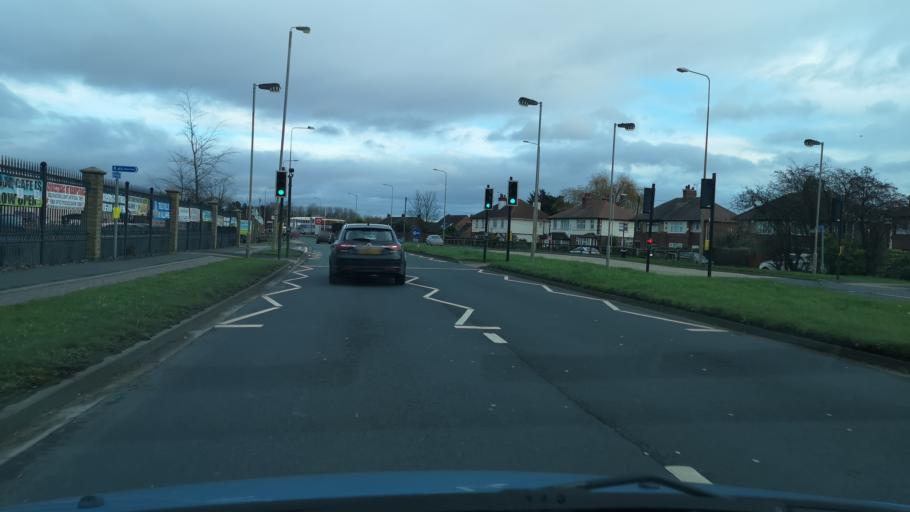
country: GB
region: England
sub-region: City and Borough of Wakefield
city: Crigglestone
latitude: 53.6528
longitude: -1.5202
